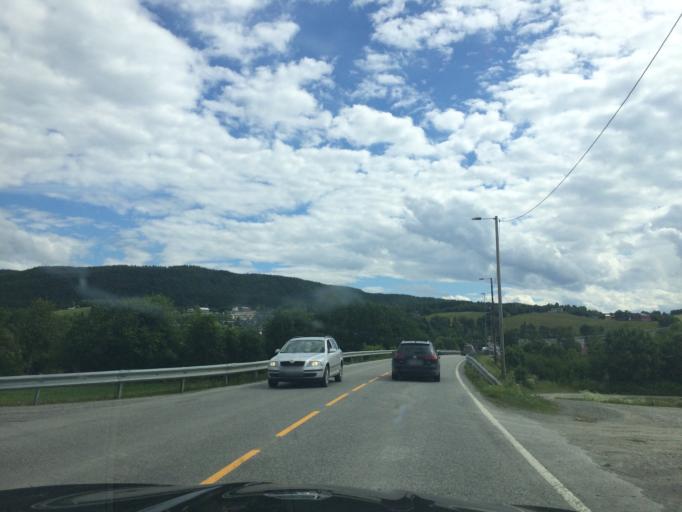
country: NO
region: Sor-Trondelag
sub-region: Selbu
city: Mebonden
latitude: 63.2537
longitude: 11.0902
